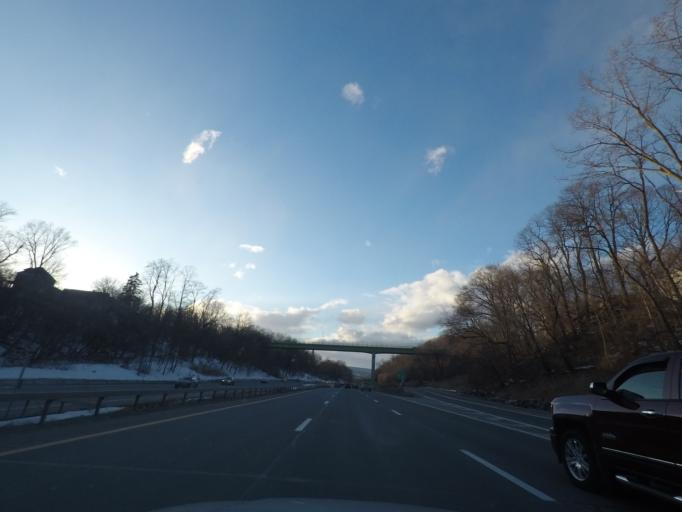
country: US
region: New York
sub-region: Schenectady County
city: Schenectady
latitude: 42.8013
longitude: -73.9413
